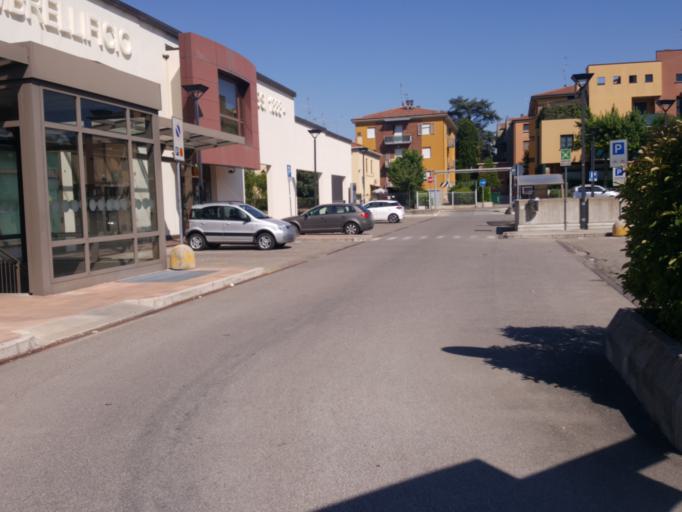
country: IT
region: Emilia-Romagna
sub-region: Provincia di Bologna
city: Castel San Pietro Terme
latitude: 44.4008
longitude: 11.5879
